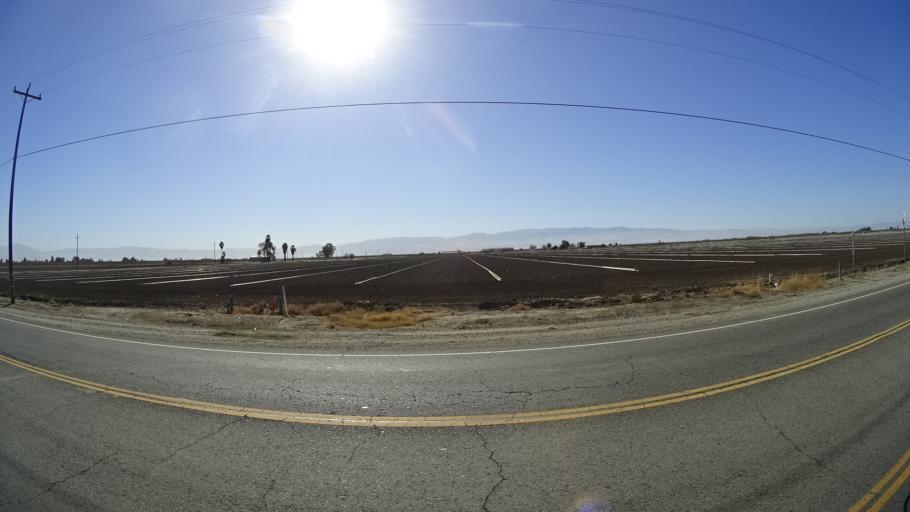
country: US
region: California
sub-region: Kern County
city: Greenfield
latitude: 35.2670
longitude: -119.0491
